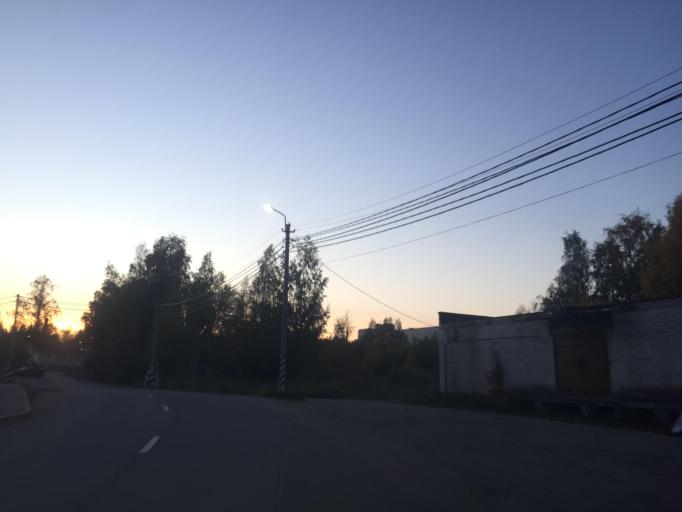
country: RU
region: Leningrad
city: Priozersk
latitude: 61.0336
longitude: 30.1267
